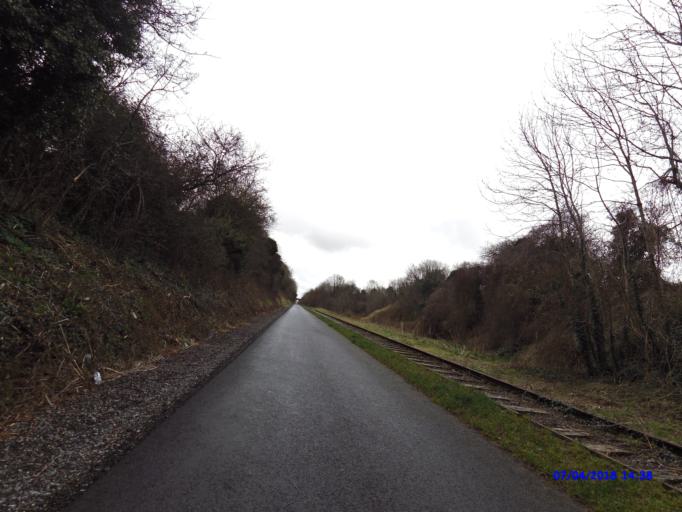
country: IE
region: Leinster
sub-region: An Iarmhi
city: Athlone
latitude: 53.4223
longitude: -7.8993
